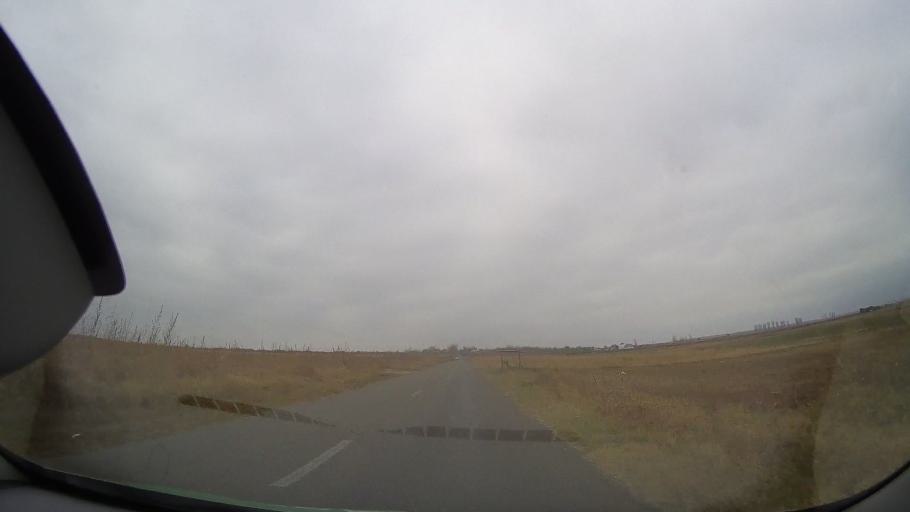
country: RO
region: Buzau
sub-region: Comuna Luciu
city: Luciu
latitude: 44.9786
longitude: 27.0498
